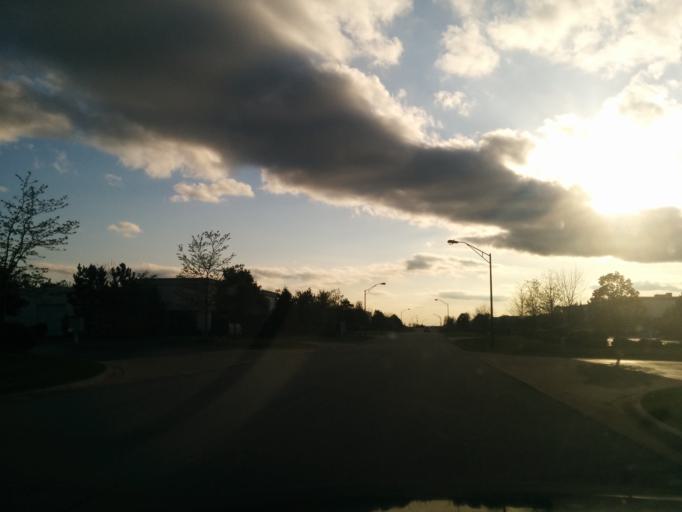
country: US
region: Illinois
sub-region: DuPage County
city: Wayne
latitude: 41.9778
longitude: -88.2180
